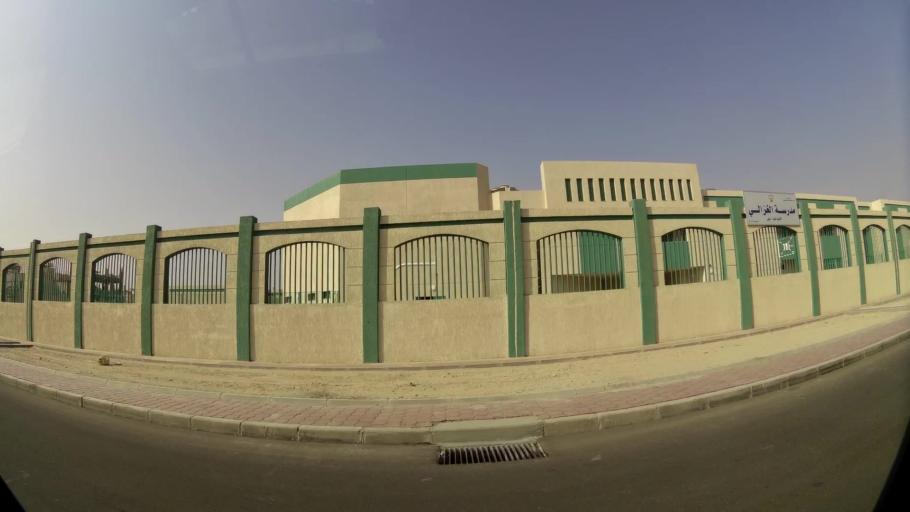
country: KW
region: Muhafazat al Jahra'
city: Al Jahra'
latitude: 29.3581
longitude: 47.7625
